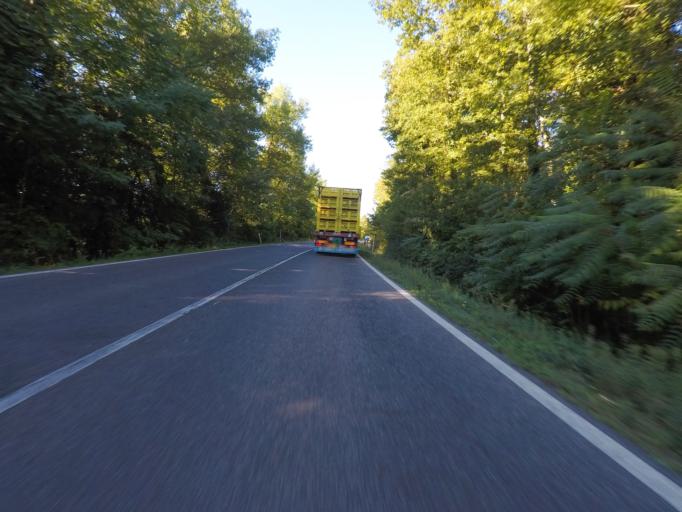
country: IT
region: Tuscany
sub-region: Provincia di Siena
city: Rosia
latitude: 43.1940
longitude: 11.2770
